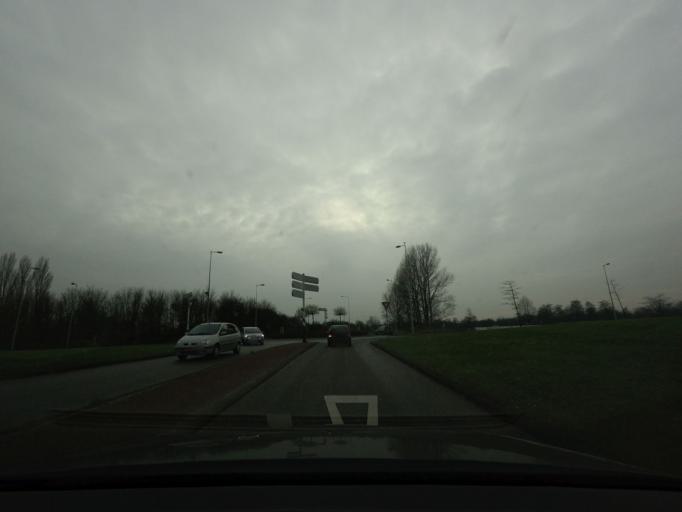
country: NL
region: North Holland
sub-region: Gemeente Amsterdam
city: Amsterdam-Zuidoost
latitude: 52.3020
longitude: 4.9788
